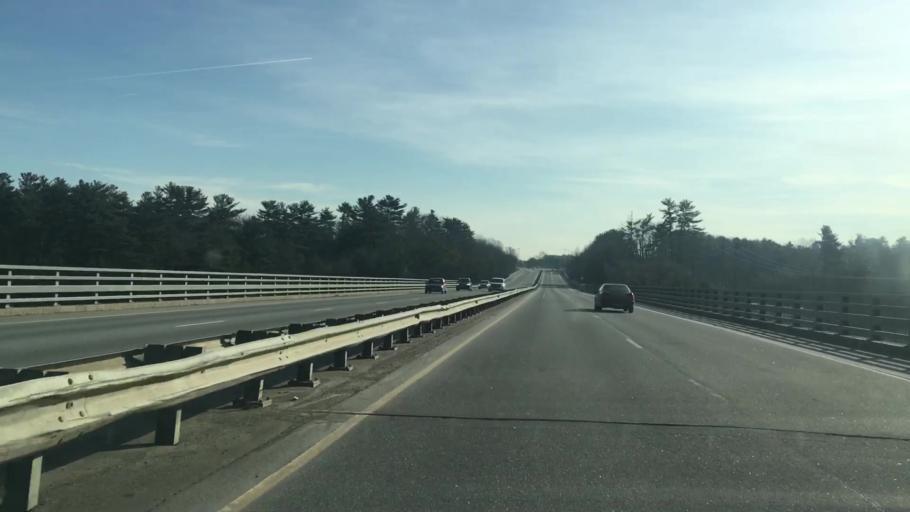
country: US
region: Maine
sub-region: Androscoggin County
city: Lewiston
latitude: 44.1172
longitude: -70.2171
